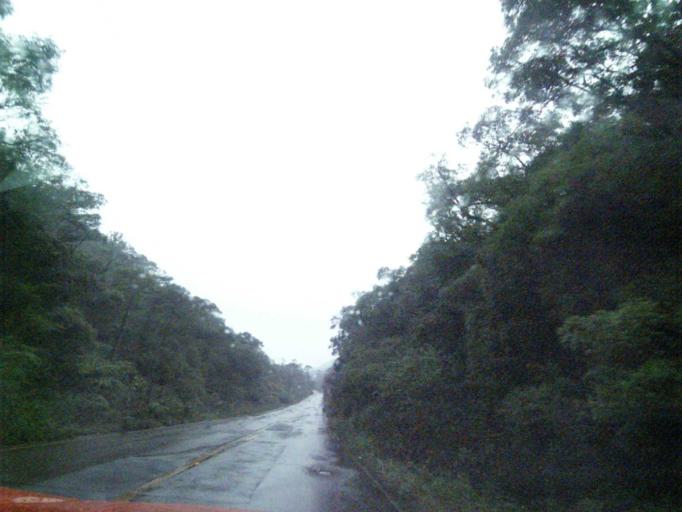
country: BR
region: Santa Catarina
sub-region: Anitapolis
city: Anitapolis
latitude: -27.7731
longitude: -49.0408
